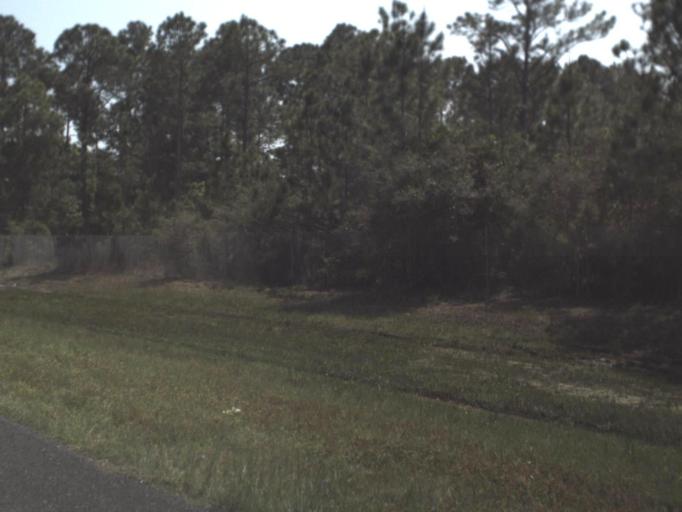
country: US
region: Florida
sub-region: Santa Rosa County
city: Tiger Point
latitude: 30.3926
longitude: -87.0676
